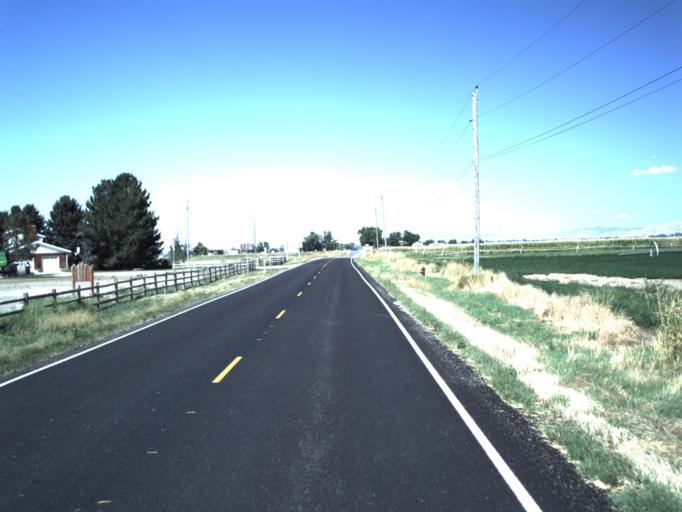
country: US
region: Utah
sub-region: Cache County
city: Lewiston
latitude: 41.9967
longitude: -111.8765
